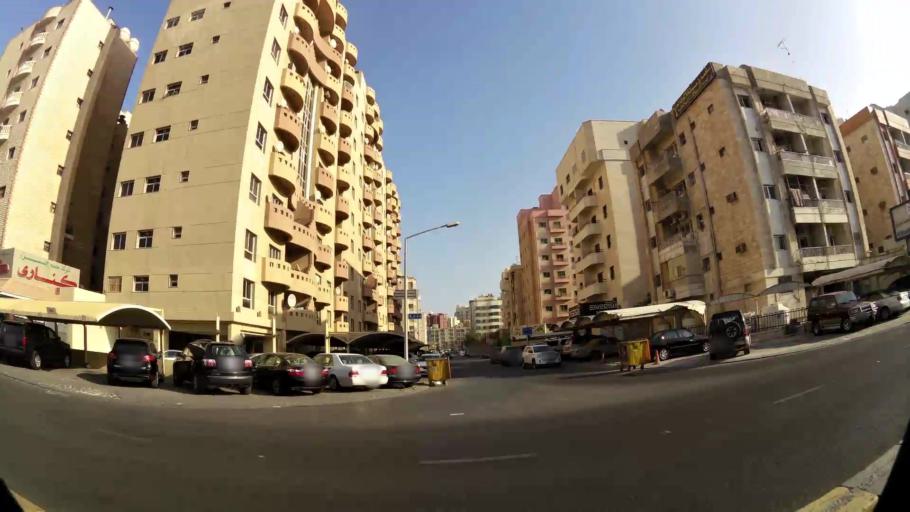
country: KW
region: Muhafazat Hawalli
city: As Salimiyah
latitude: 29.3358
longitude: 48.0861
